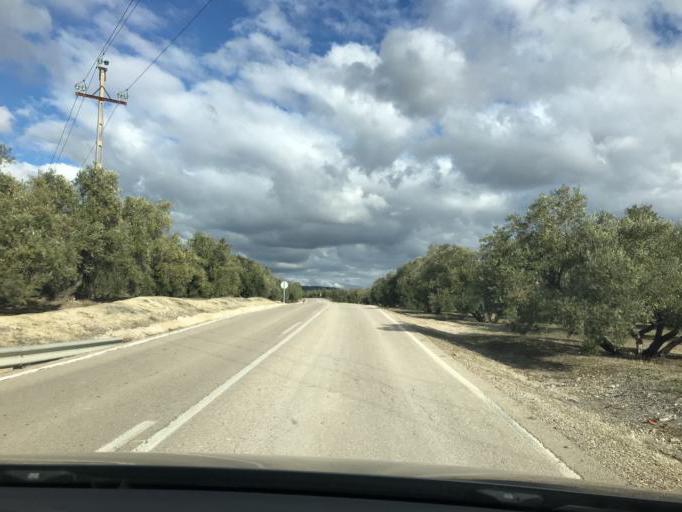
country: ES
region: Andalusia
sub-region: Provincia de Jaen
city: Ubeda
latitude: 37.9904
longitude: -3.3900
